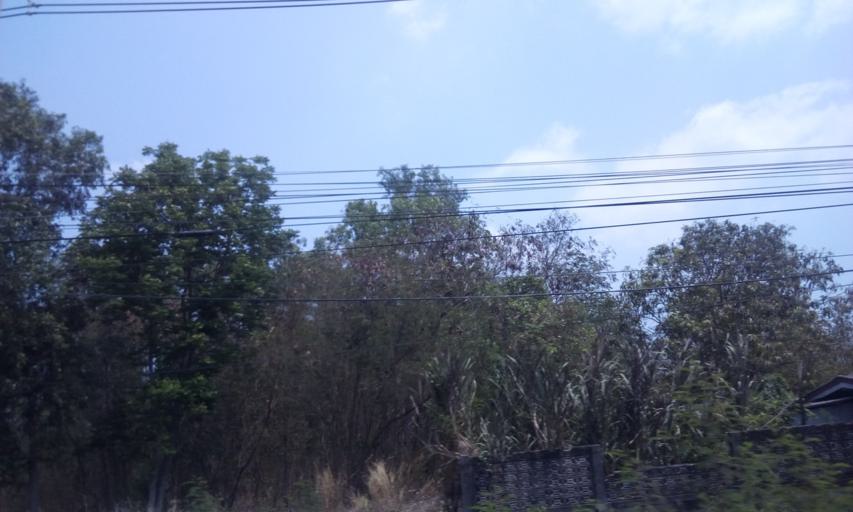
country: TH
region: Chachoengsao
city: Chachoengsao
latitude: 13.7333
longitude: 101.0870
